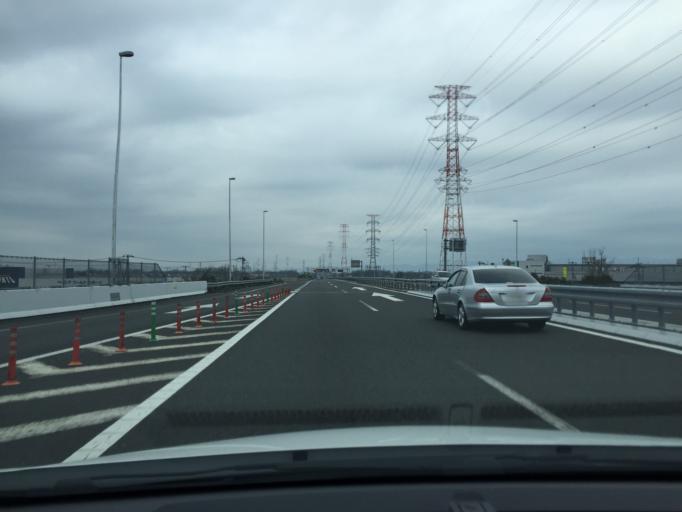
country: JP
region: Saitama
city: Kawagoe
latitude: 35.9816
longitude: 139.4664
